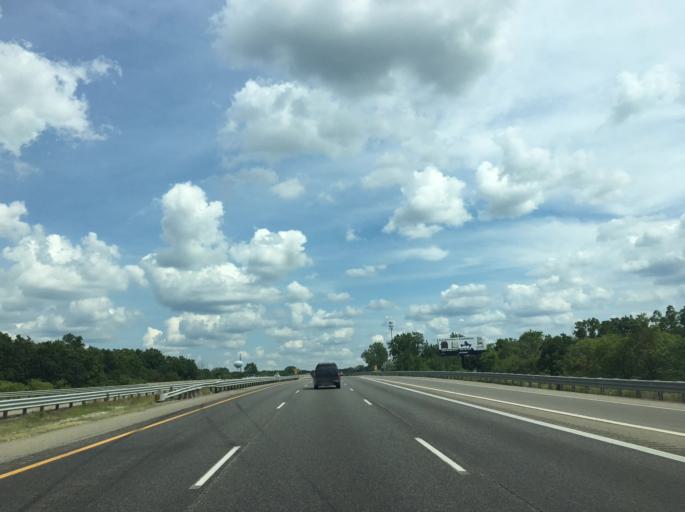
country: US
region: Michigan
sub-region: Genesee County
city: Grand Blanc
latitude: 42.8939
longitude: -83.6300
